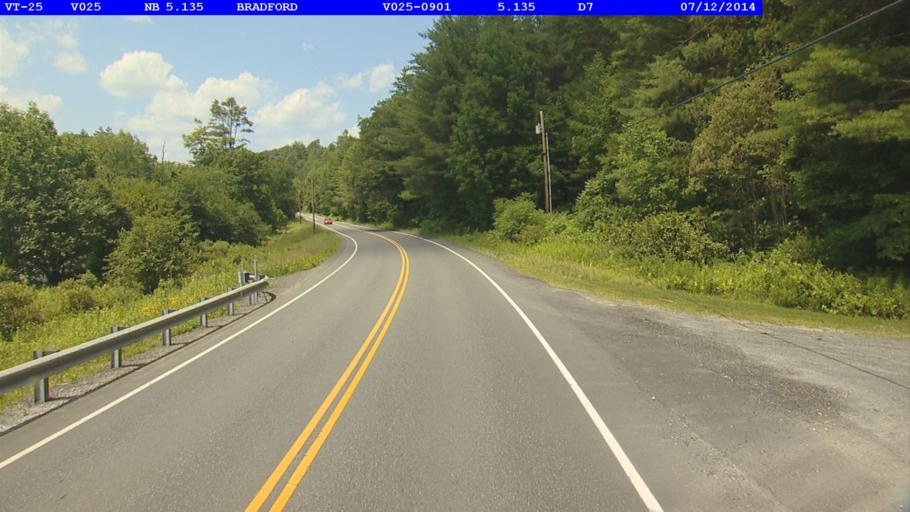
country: US
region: New Hampshire
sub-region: Grafton County
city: Haverhill
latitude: 44.0264
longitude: -72.1759
